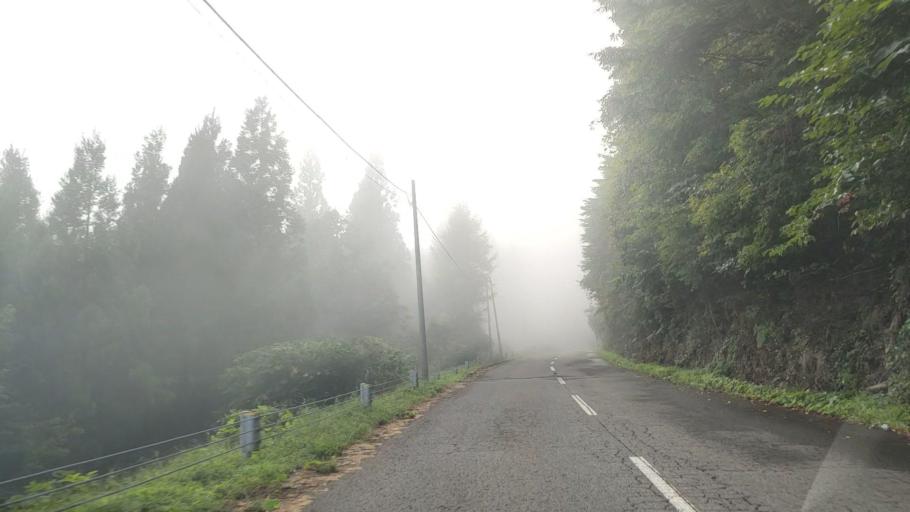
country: JP
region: Nagano
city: Iiyama
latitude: 36.8226
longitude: 138.4191
